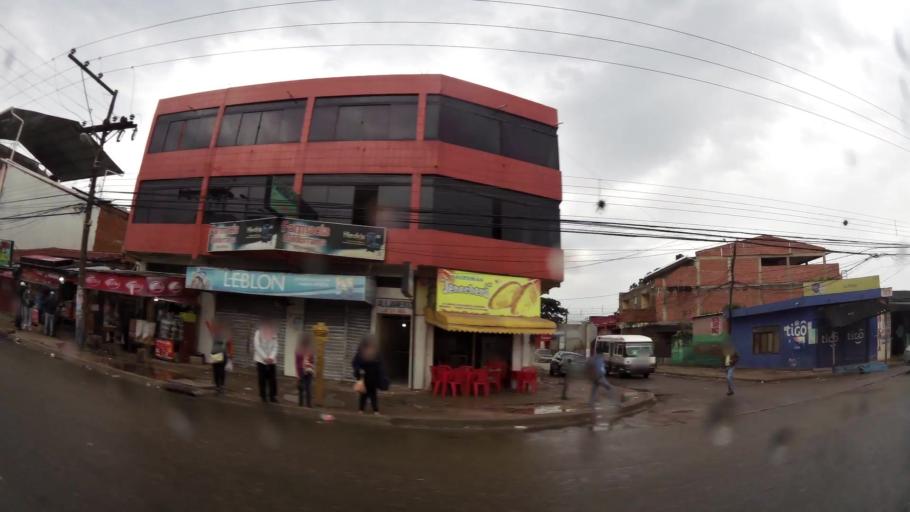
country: BO
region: Santa Cruz
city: Santa Cruz de la Sierra
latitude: -17.7715
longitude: -63.1253
